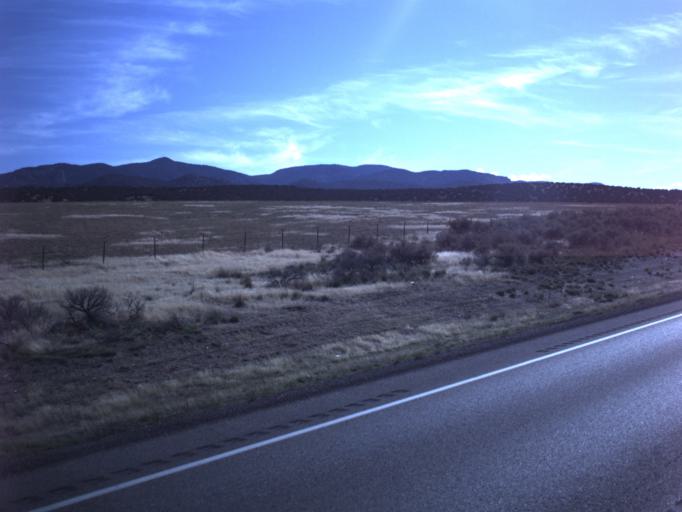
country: US
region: Utah
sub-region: Sanpete County
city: Gunnison
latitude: 39.3372
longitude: -111.9192
